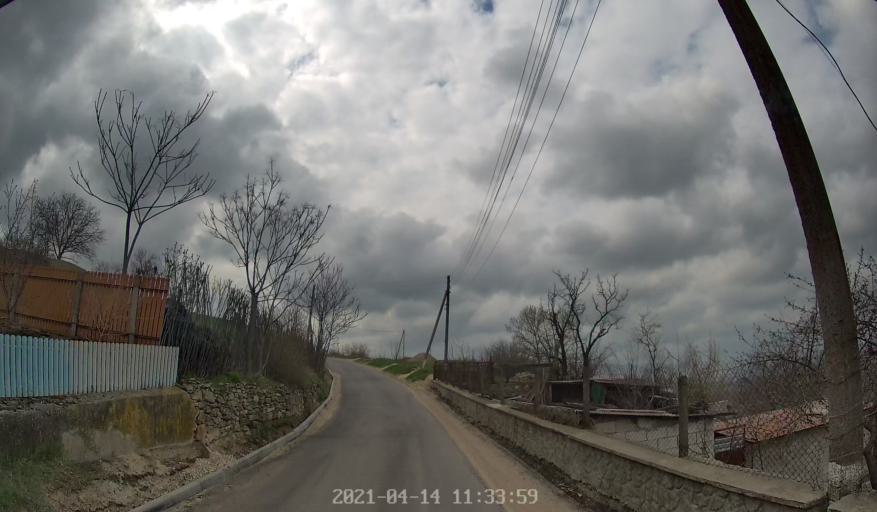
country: MD
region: Criuleni
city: Criuleni
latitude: 47.1774
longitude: 29.1645
